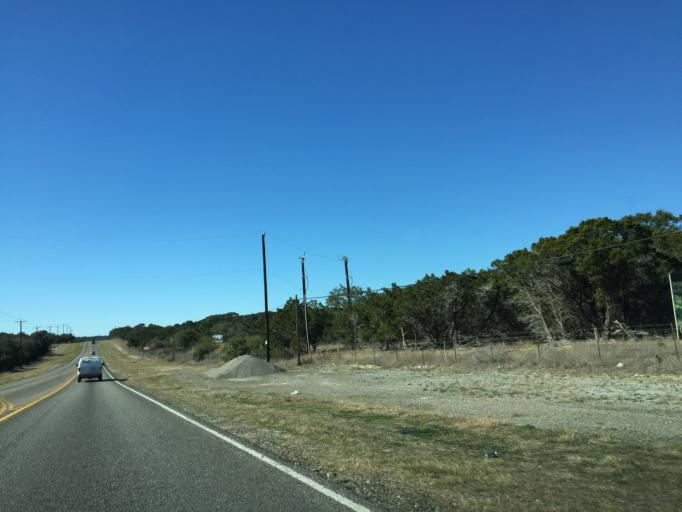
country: US
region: Texas
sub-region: Comal County
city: Garden Ridge
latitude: 29.6987
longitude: -98.3224
